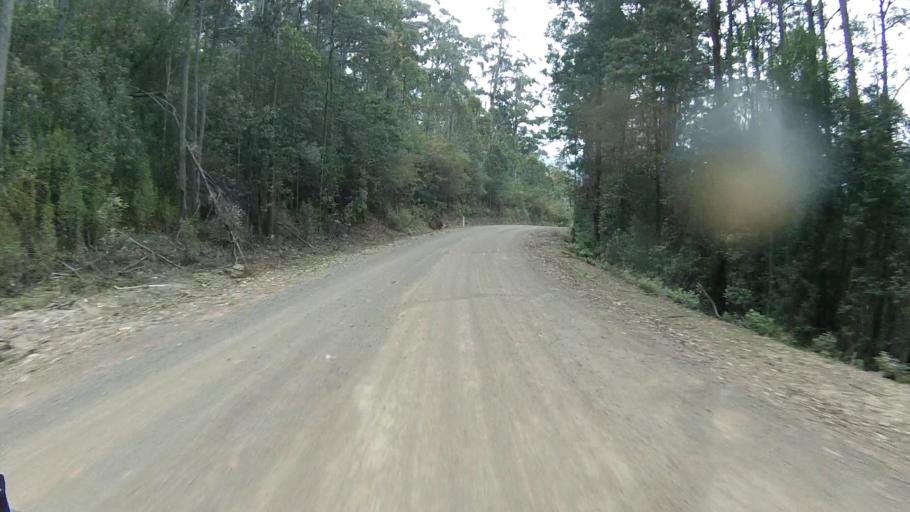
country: AU
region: Tasmania
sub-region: Sorell
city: Sorell
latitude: -42.6986
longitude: 147.8548
